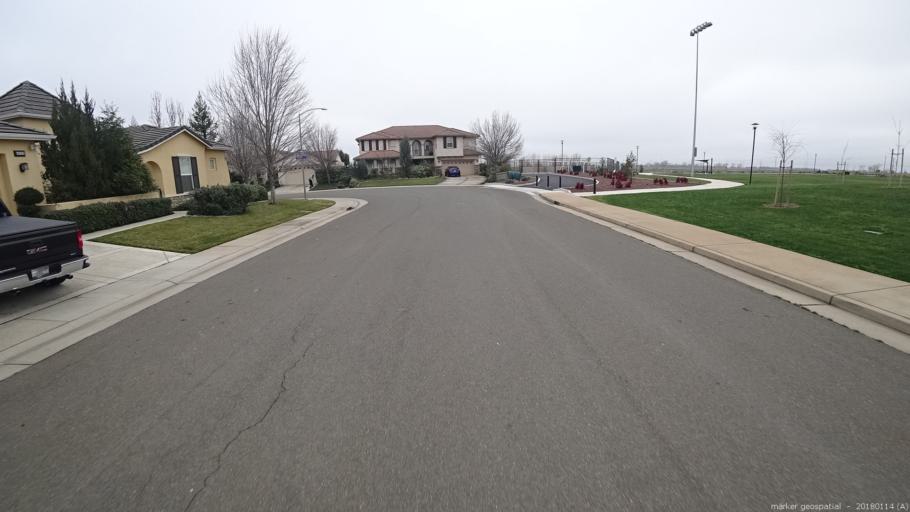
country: US
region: California
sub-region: Sacramento County
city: Rancho Cordova
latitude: 38.5379
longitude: -121.2386
